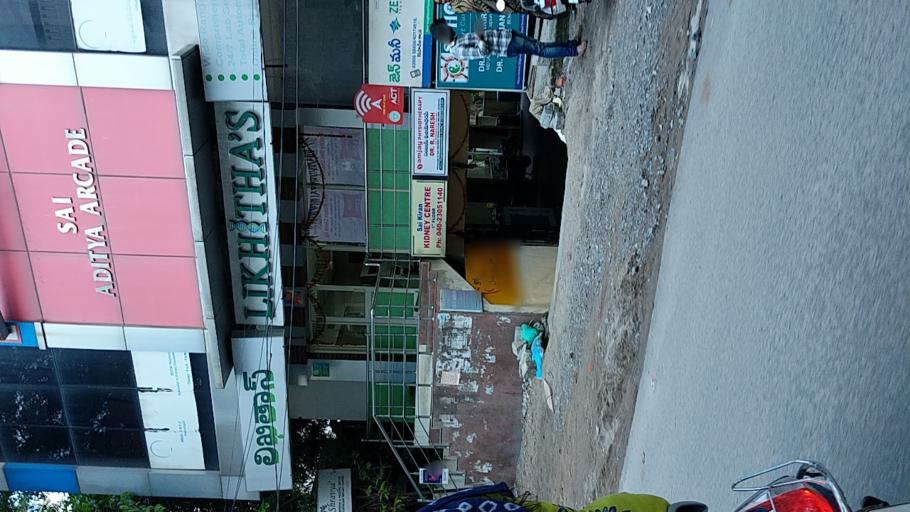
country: IN
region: Telangana
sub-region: Rangareddi
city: Kukatpalli
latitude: 17.4933
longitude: 78.3980
